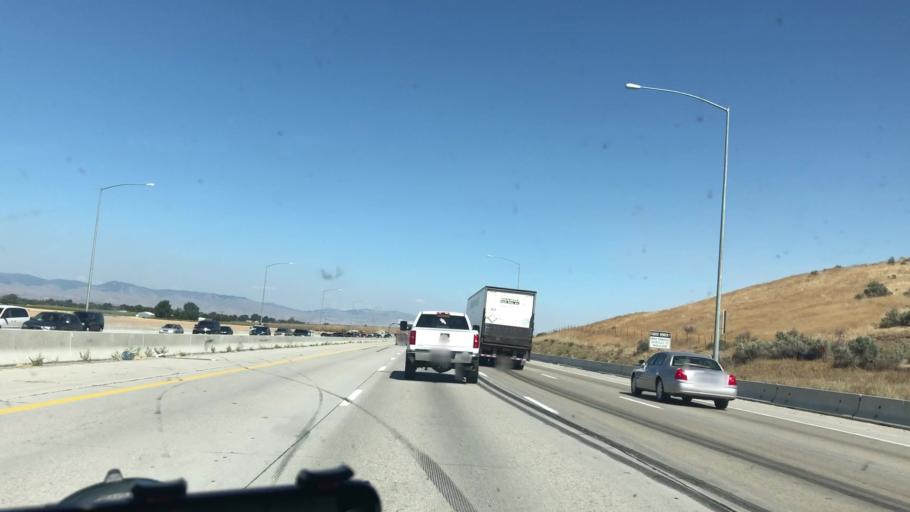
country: US
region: Idaho
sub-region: Canyon County
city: Nampa
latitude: 43.5995
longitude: -116.5044
